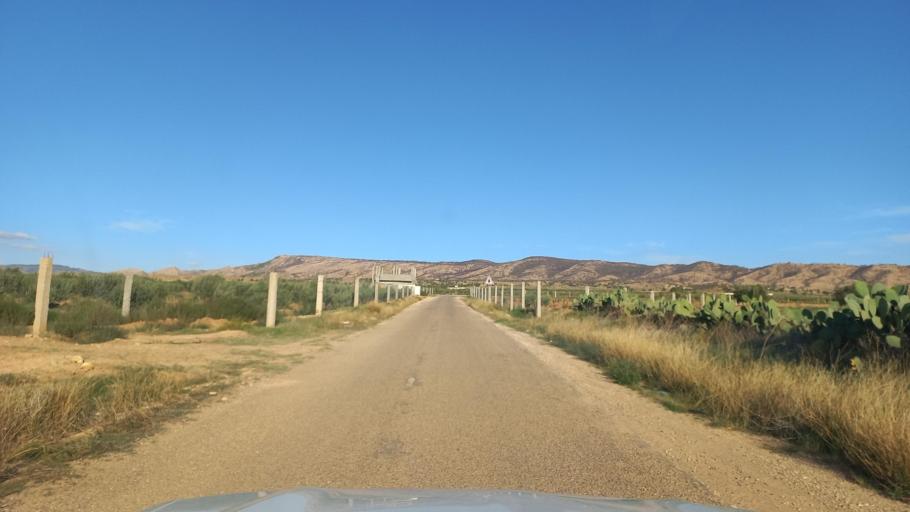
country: TN
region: Al Qasrayn
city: Sbiba
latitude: 35.3370
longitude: 9.1167
